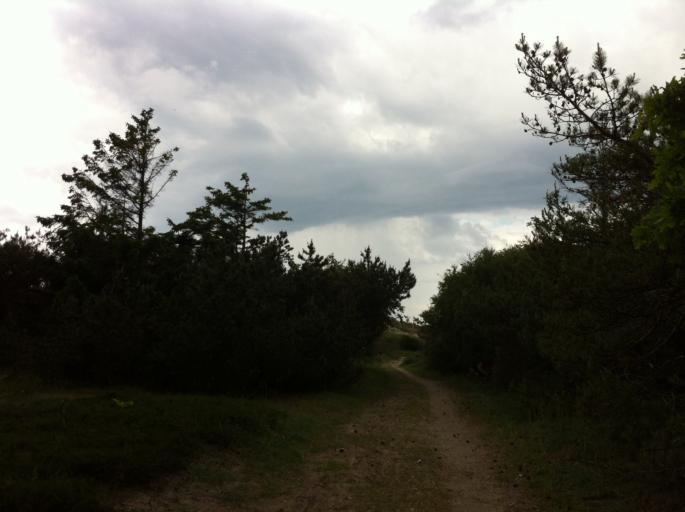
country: DK
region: Capital Region
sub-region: Halsnaes Kommune
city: Frederiksvaerk
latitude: 56.0402
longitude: 12.0330
